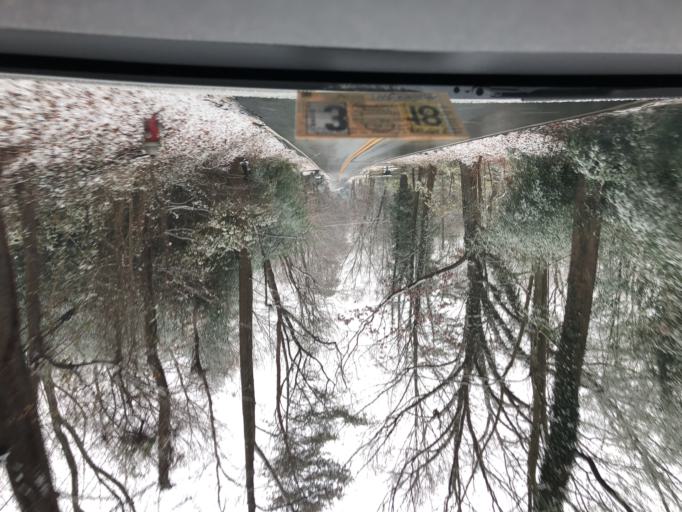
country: US
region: Virginia
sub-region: Fairfax County
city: Oakton
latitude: 38.9039
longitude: -77.2999
